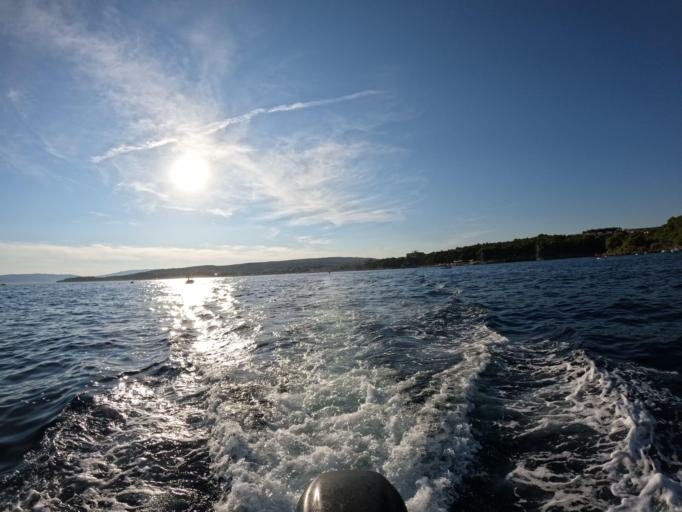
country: HR
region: Primorsko-Goranska
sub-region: Grad Krk
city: Krk
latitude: 45.0208
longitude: 14.5891
